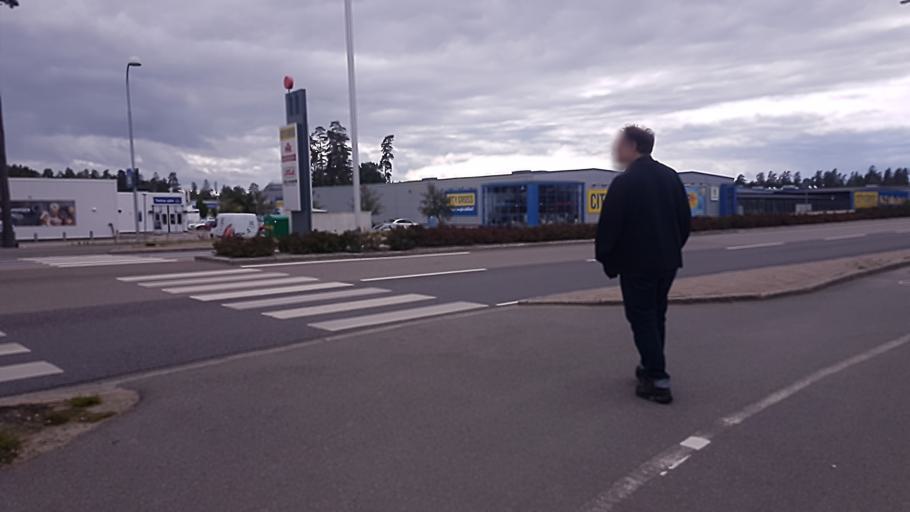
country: SE
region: Kronoberg
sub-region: Vaxjo Kommun
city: Vaexjoe
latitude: 56.8791
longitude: 14.7750
